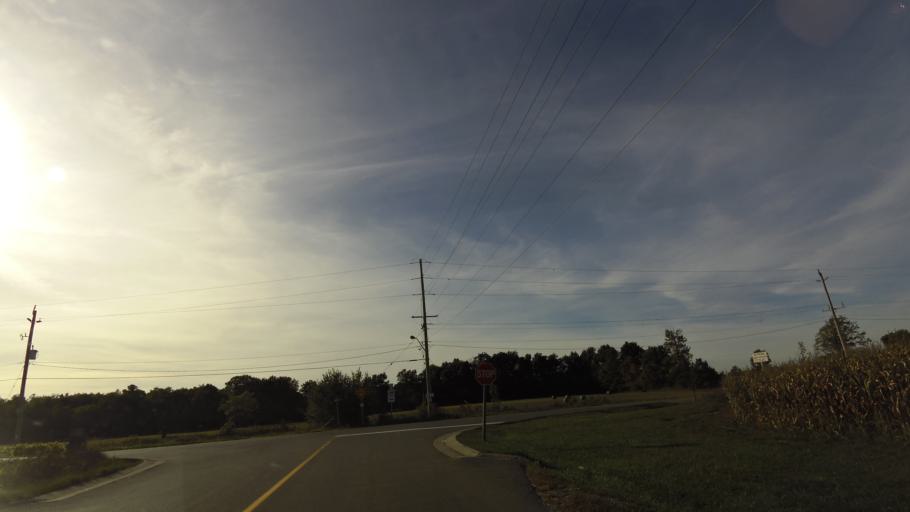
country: CA
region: Ontario
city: Ancaster
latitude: 43.0949
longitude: -79.9679
